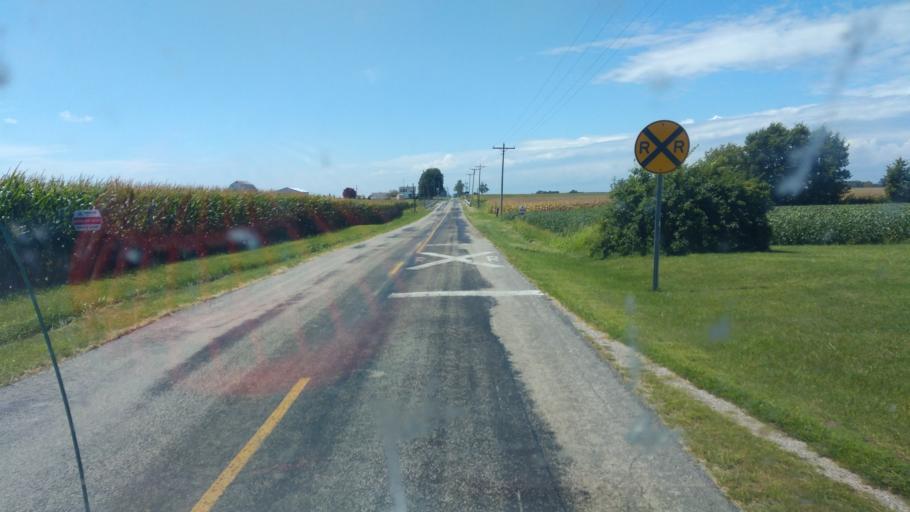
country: US
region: Ohio
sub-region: Marion County
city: Marion
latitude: 40.6587
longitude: -83.1887
